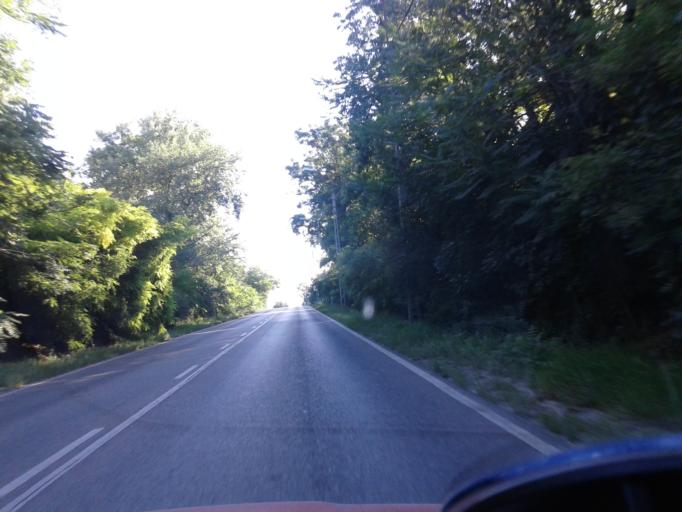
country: HU
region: Budapest
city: Budapest XI. keruelet
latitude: 47.4607
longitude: 19.0106
